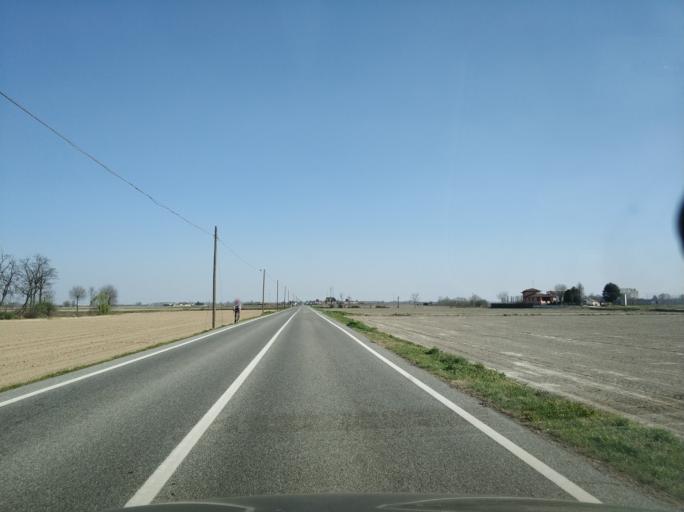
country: IT
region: Piedmont
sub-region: Provincia di Vercelli
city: Borgo Vercelli
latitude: 45.3218
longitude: 8.4797
